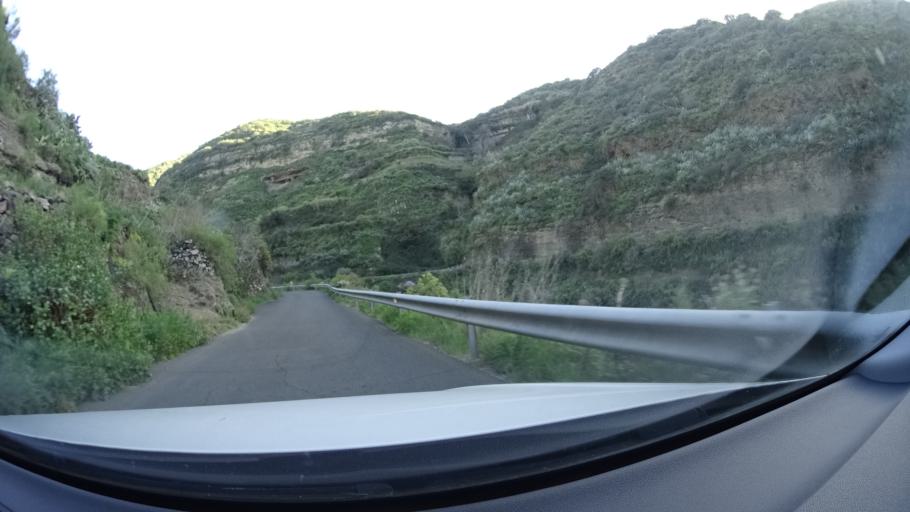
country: ES
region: Canary Islands
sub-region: Provincia de Las Palmas
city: Artenara
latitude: 28.0464
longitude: -15.6653
